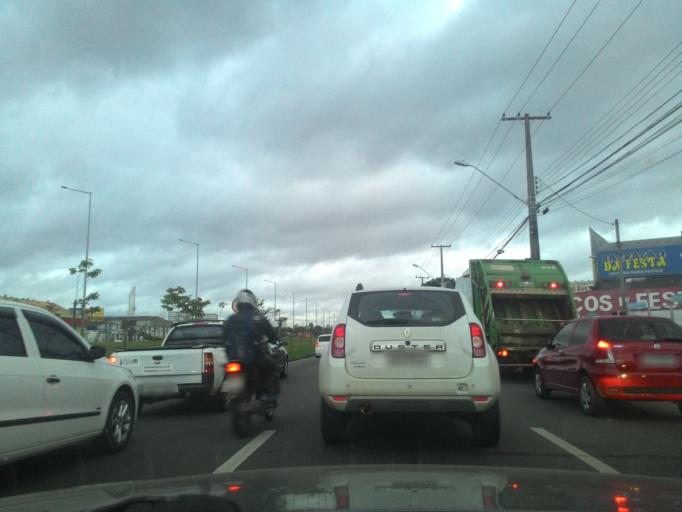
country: BR
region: Parana
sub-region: Curitiba
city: Curitiba
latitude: -25.4744
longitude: -49.2575
